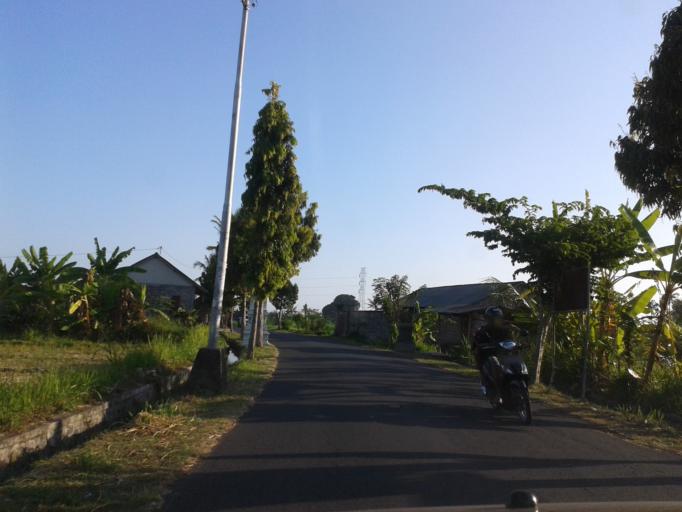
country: ID
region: Bali
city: Semarapura
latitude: -8.5600
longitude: 115.3867
